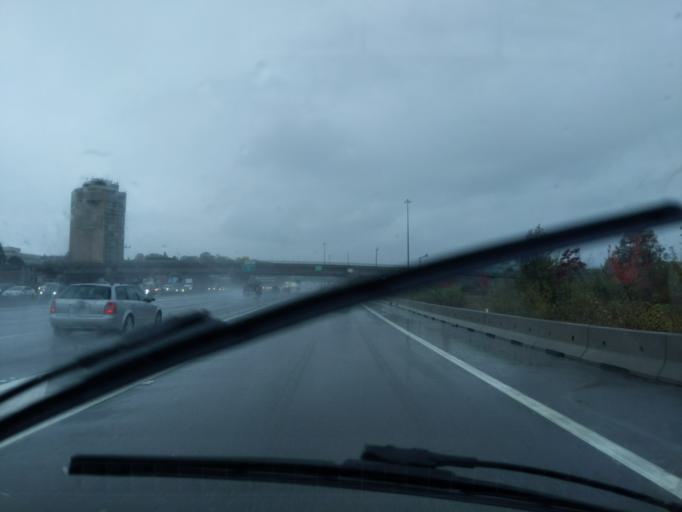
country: CA
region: British Columbia
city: Burnaby
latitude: 49.2579
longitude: -123.0017
